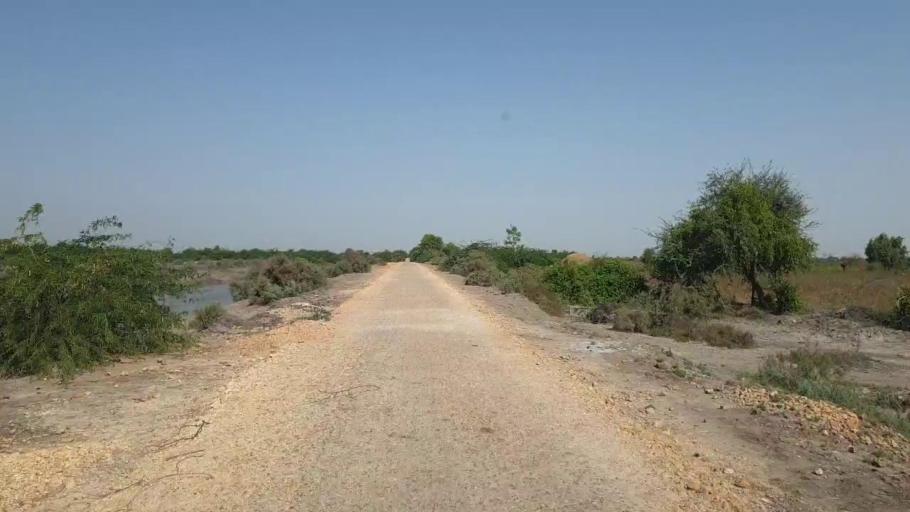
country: PK
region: Sindh
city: Tando Bago
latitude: 24.7230
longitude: 69.0733
